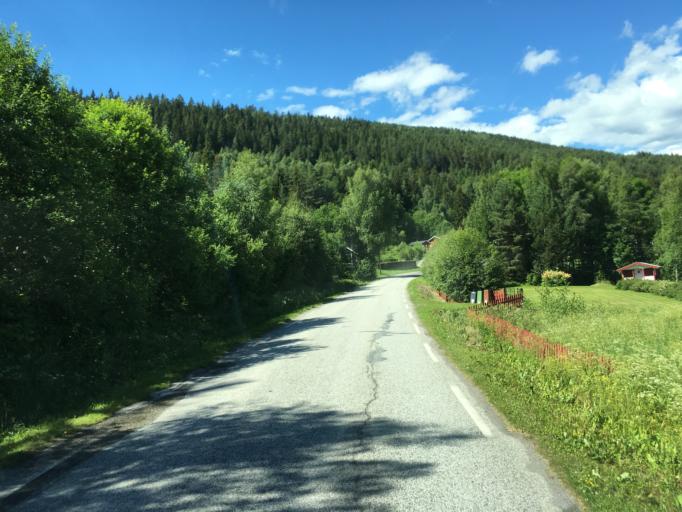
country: NO
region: Oppland
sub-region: Jevnaker
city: Jevnaker
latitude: 60.3103
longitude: 10.3446
